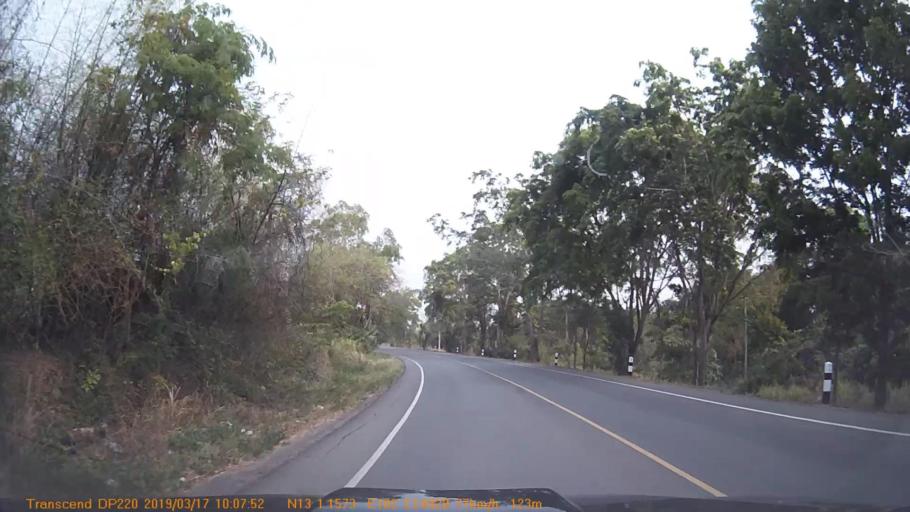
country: TH
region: Chanthaburi
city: Pong Nam Ron
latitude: 13.0216
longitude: 102.3975
